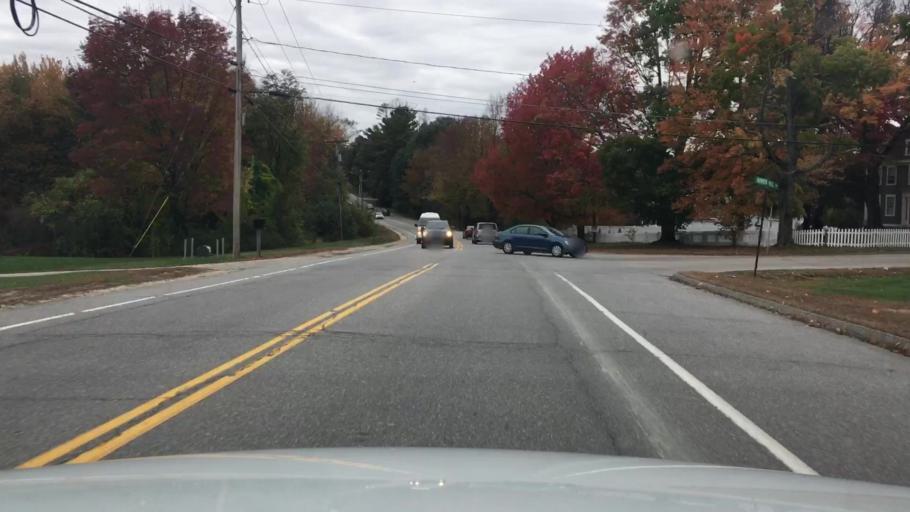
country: US
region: New Hampshire
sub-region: Strafford County
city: Somersworth
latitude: 43.2721
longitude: -70.9119
